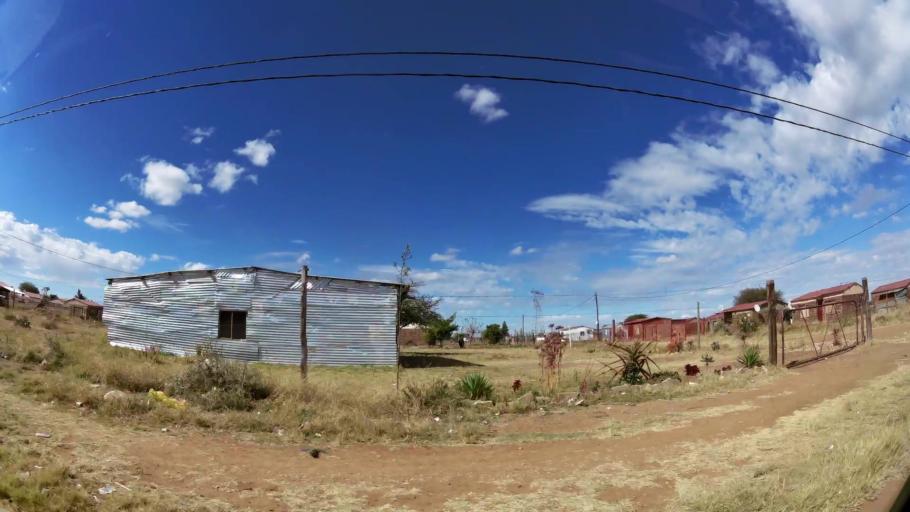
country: ZA
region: Limpopo
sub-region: Waterberg District Municipality
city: Bela-Bela
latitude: -24.8850
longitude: 28.3322
